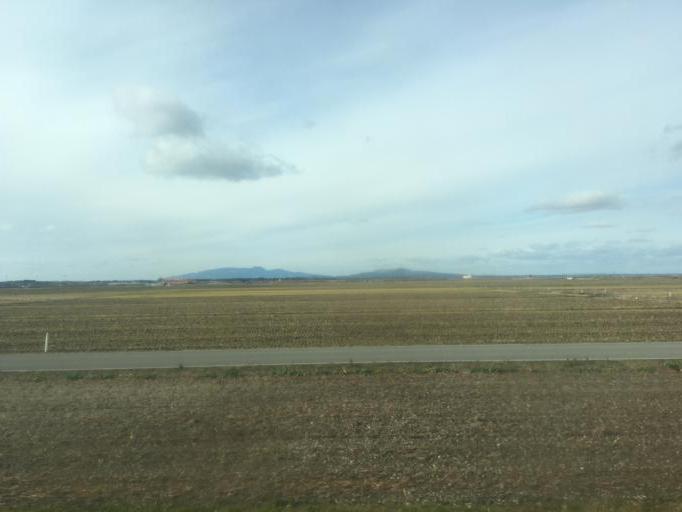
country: JP
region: Akita
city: Tenno
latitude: 39.8746
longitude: 140.0642
